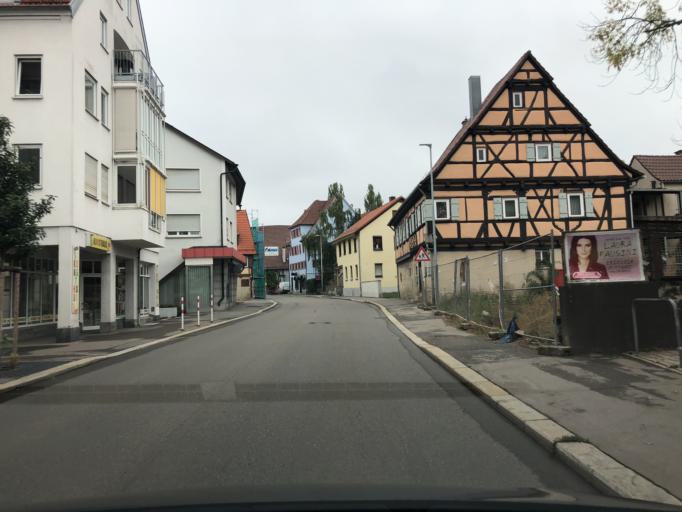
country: DE
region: Baden-Wuerttemberg
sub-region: Regierungsbezirk Stuttgart
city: Sindelfingen
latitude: 48.7115
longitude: 9.0003
